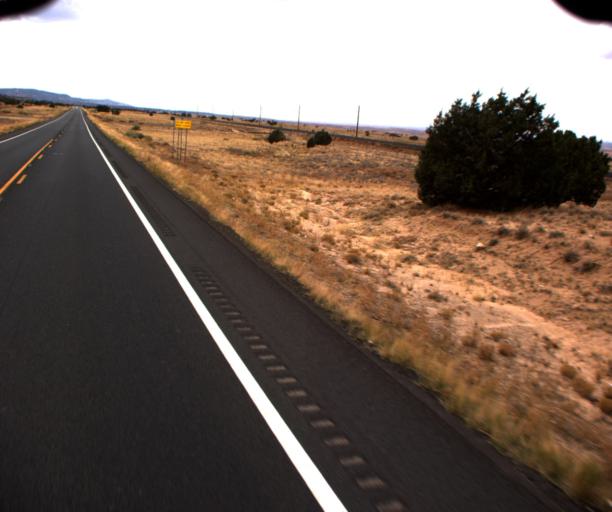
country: US
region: Arizona
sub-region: Navajo County
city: Kayenta
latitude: 36.4896
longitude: -110.6342
